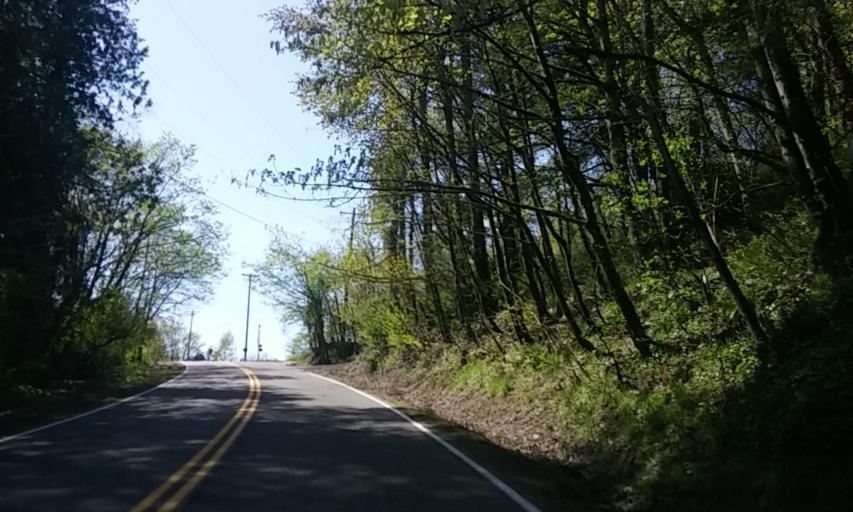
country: US
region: Oregon
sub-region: Washington County
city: West Haven
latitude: 45.5327
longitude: -122.7533
